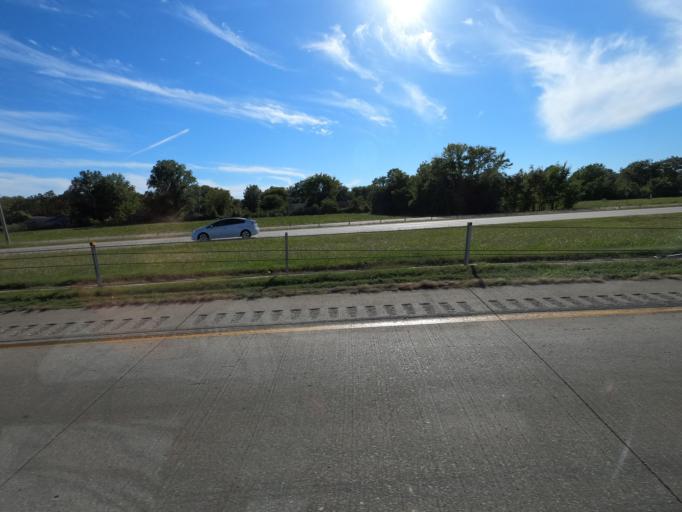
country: US
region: Arkansas
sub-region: Crittenden County
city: West Memphis
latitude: 35.1533
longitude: -90.1446
